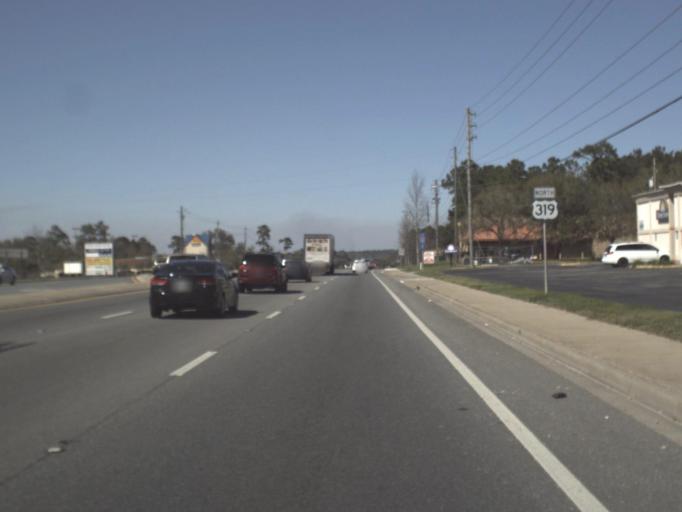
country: US
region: Florida
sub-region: Leon County
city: Tallahassee
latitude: 30.4282
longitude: -84.2266
